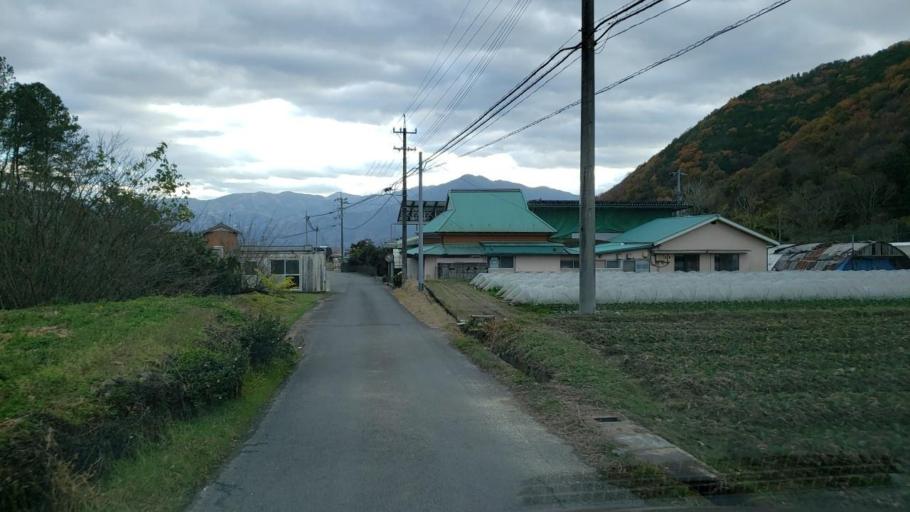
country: JP
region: Tokushima
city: Wakimachi
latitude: 34.1090
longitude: 134.2241
